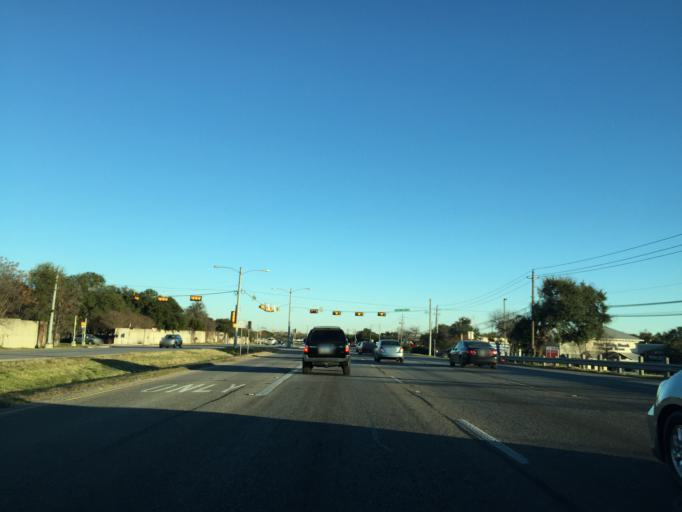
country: US
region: Texas
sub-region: Travis County
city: Wells Branch
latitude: 30.4258
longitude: -97.7161
